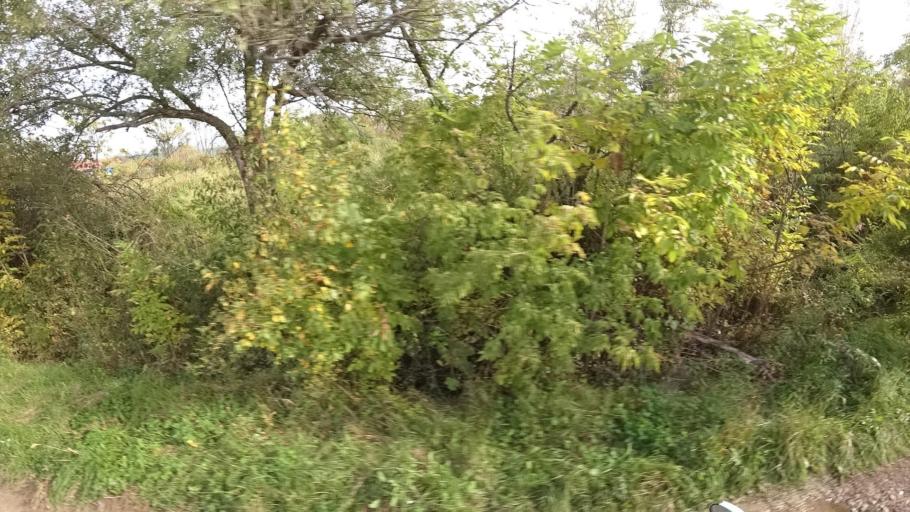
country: RU
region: Primorskiy
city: Dostoyevka
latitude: 44.2933
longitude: 133.4253
